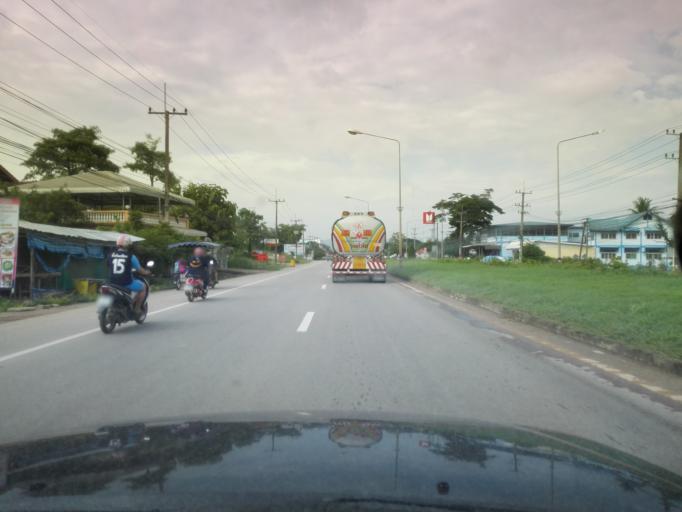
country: TH
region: Tak
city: Mae Sot
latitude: 16.7157
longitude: 98.5575
